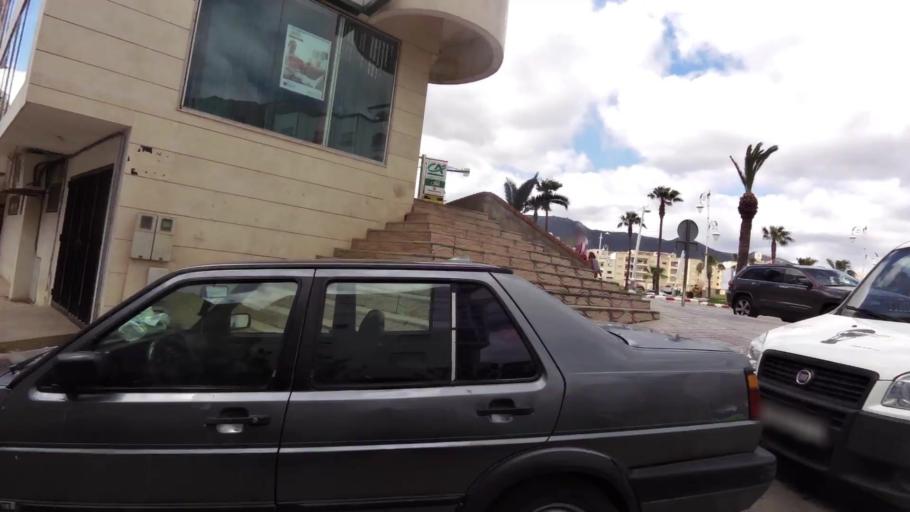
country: MA
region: Tanger-Tetouan
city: Tetouan
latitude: 35.5892
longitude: -5.3447
